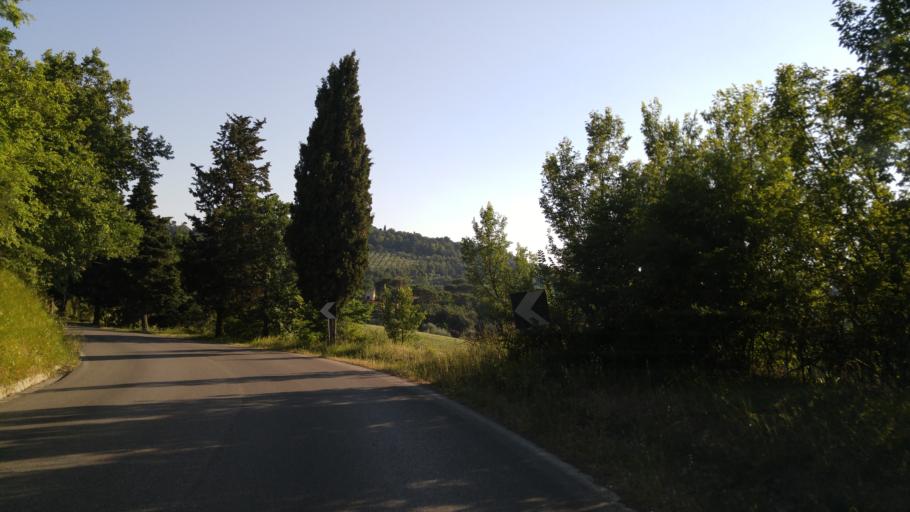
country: IT
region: The Marches
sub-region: Provincia di Pesaro e Urbino
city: Fenile
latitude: 43.8682
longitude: 12.9369
